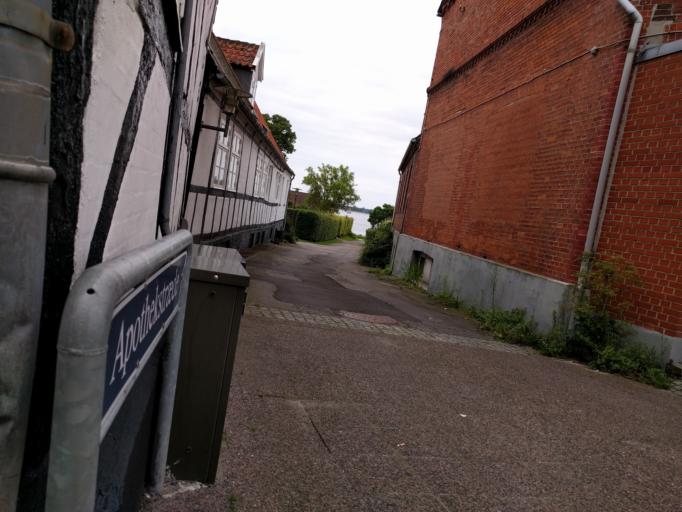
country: DK
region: Zealand
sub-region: Guldborgsund Kommune
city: Stubbekobing
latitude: 54.8903
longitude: 12.0395
